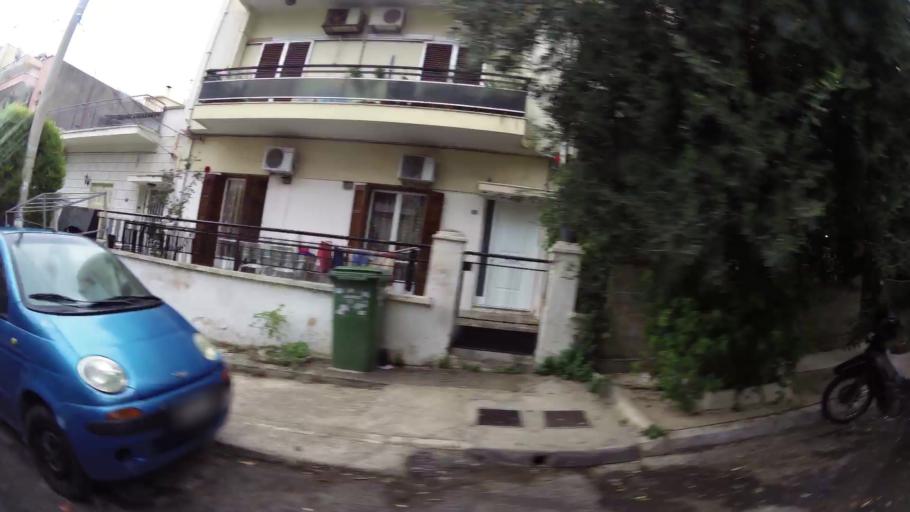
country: GR
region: Attica
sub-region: Nomos Piraios
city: Korydallos
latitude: 37.9881
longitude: 23.6405
